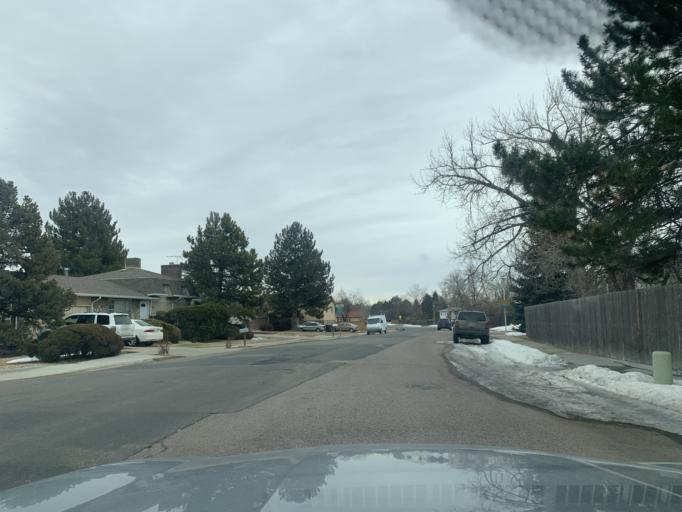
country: US
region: Colorado
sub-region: Arapahoe County
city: Glendale
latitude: 39.6616
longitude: -104.8802
